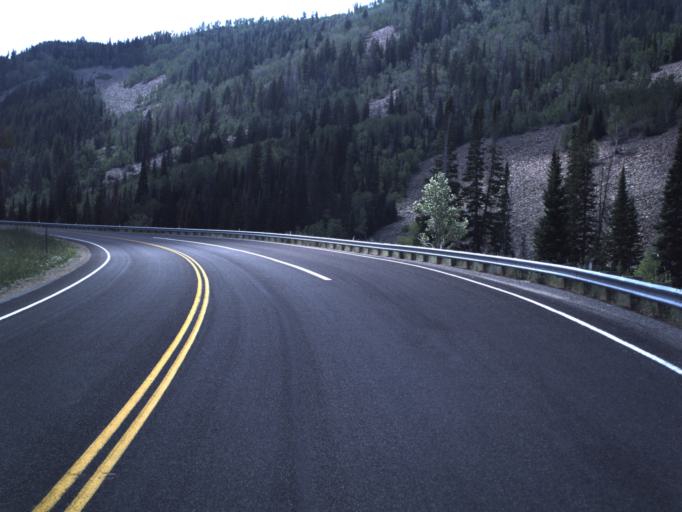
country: US
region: Utah
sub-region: Summit County
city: Francis
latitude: 40.5367
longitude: -111.0993
